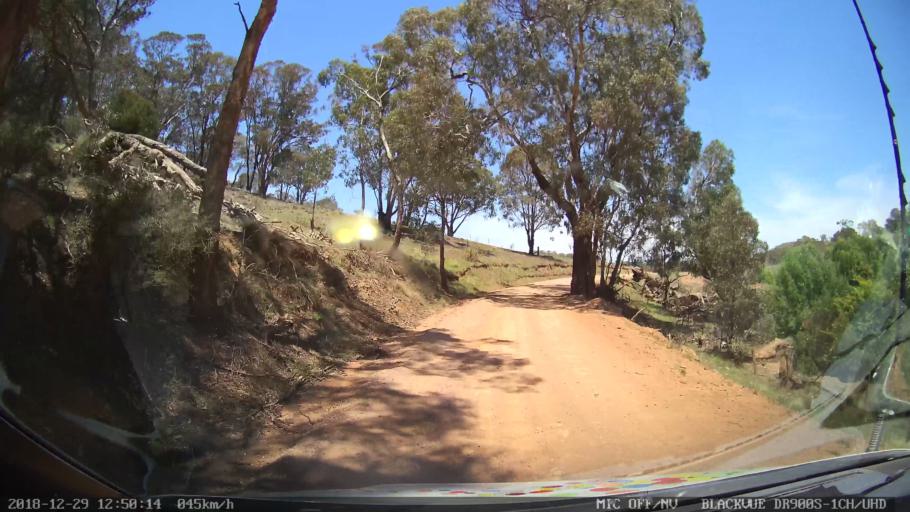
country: AU
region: Australian Capital Territory
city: Macarthur
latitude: -35.6692
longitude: 149.2038
